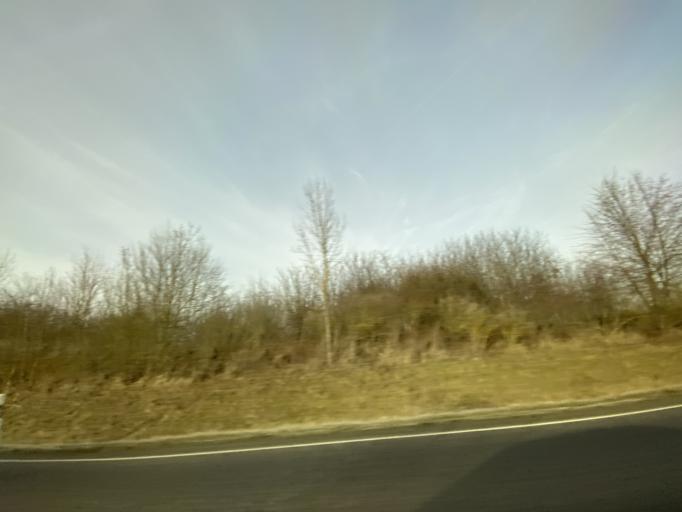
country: DE
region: Hesse
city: Amoneburg
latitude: 50.7730
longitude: 8.8878
